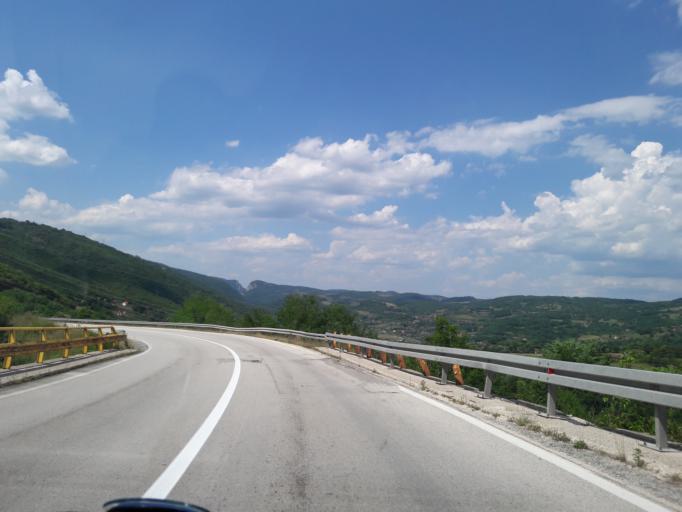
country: BA
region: Republika Srpska
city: Mrkonjic Grad
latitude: 44.5090
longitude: 17.1564
